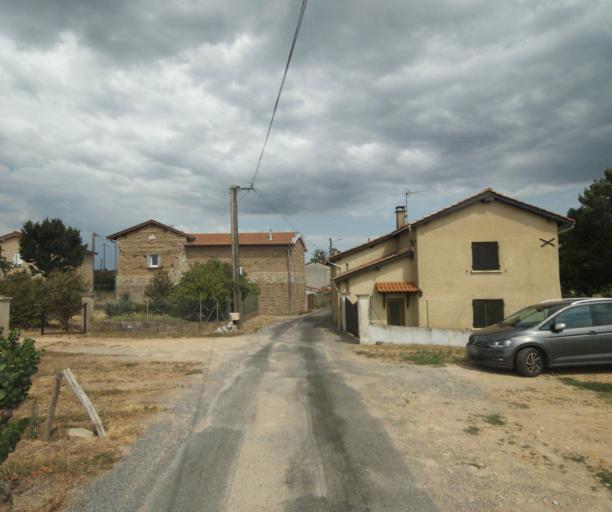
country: FR
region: Rhone-Alpes
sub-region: Departement du Rhone
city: Bully
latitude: 45.8682
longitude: 4.5552
